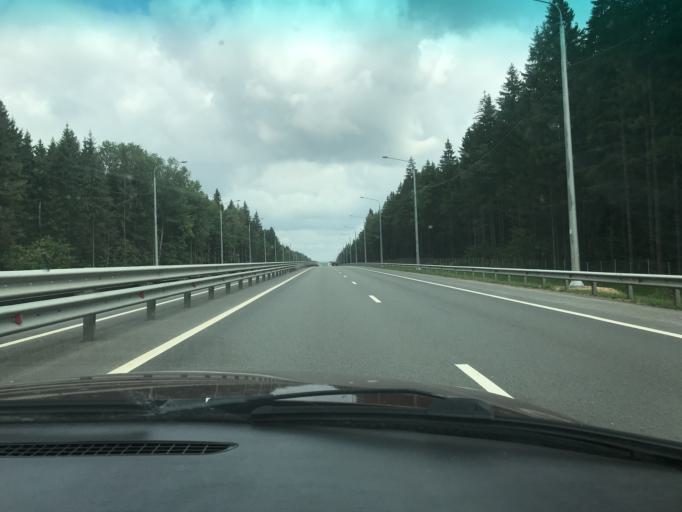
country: RU
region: Kaluga
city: Pyatovskiy
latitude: 54.6958
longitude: 36.1570
